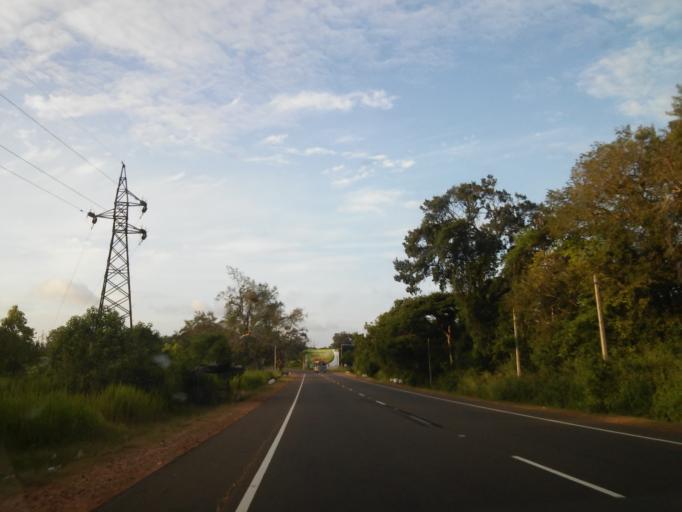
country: LK
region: North Central
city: Anuradhapura
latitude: 8.1828
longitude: 80.5284
